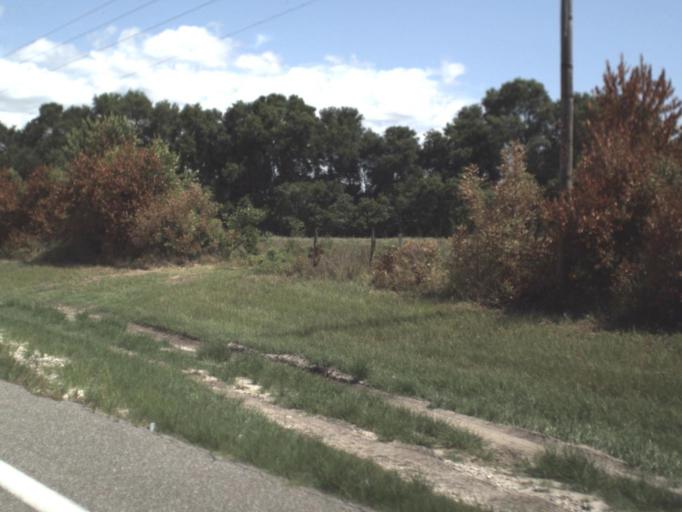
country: US
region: Florida
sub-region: Lafayette County
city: Mayo
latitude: 30.0004
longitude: -83.0204
